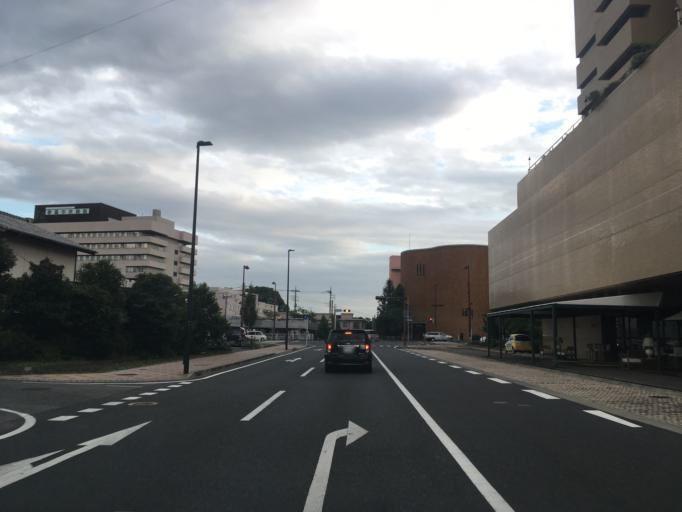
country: JP
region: Gunma
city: Maebashi-shi
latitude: 36.3881
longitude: 139.0596
